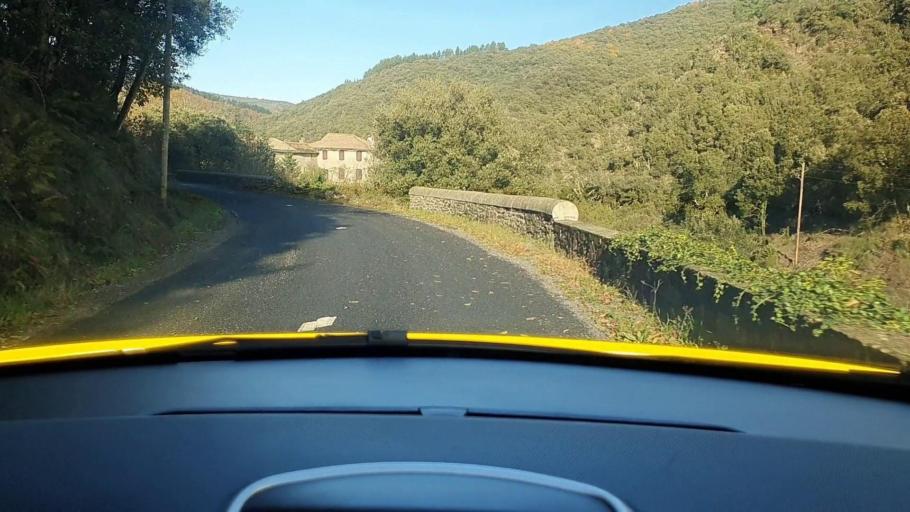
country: FR
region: Languedoc-Roussillon
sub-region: Departement du Gard
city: Valleraugue
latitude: 44.1035
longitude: 3.7325
